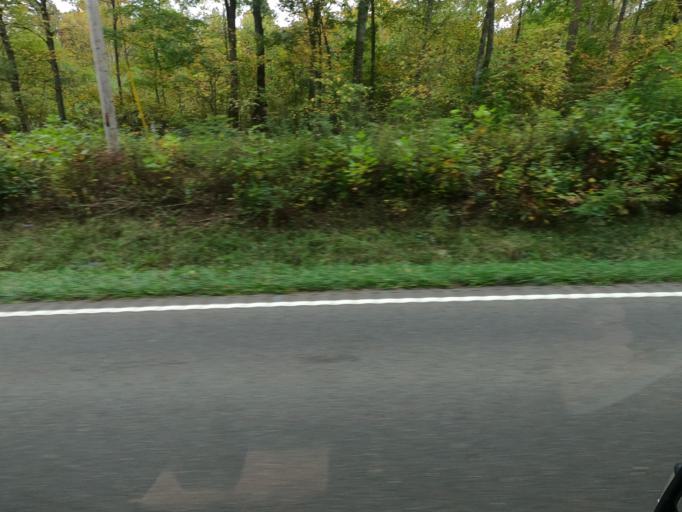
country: US
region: Tennessee
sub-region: Carter County
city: Elizabethton
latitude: 36.2604
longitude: -82.2130
